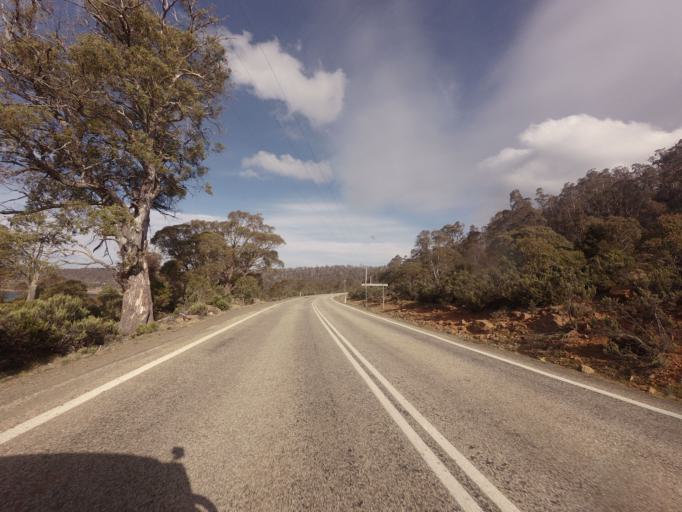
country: AU
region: Tasmania
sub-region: Meander Valley
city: Deloraine
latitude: -41.9832
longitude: 146.6793
